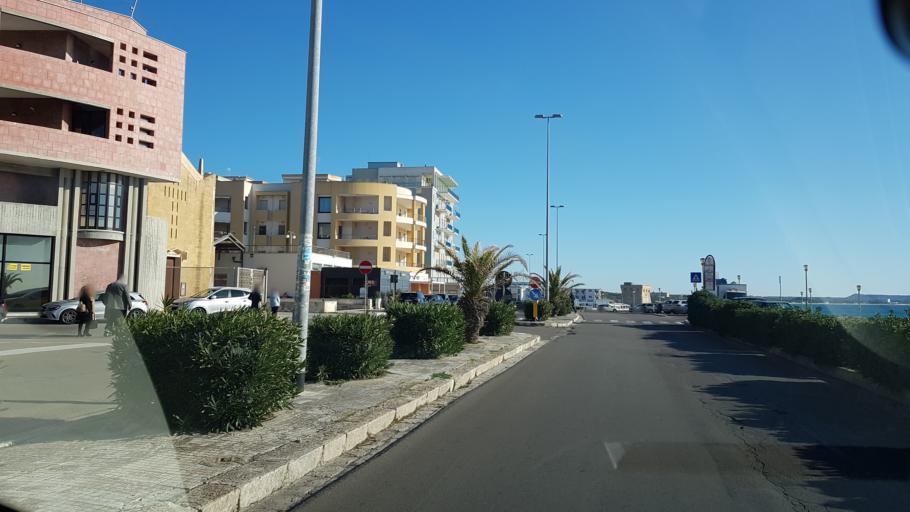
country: IT
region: Apulia
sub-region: Provincia di Lecce
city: Gallipoli
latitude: 40.0498
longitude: 18.0000
